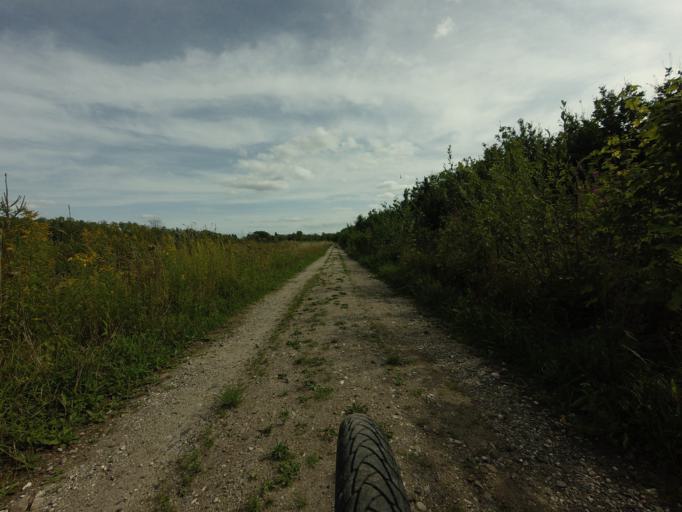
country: DK
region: Zealand
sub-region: Faxe Kommune
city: Fakse Ladeplads
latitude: 55.2283
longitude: 12.1881
